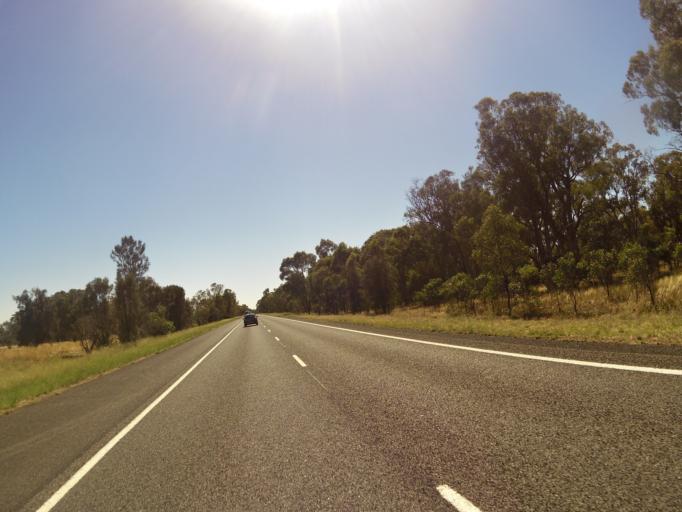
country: AU
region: Victoria
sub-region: Greater Shepparton
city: Shepparton
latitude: -36.8695
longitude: 145.2892
